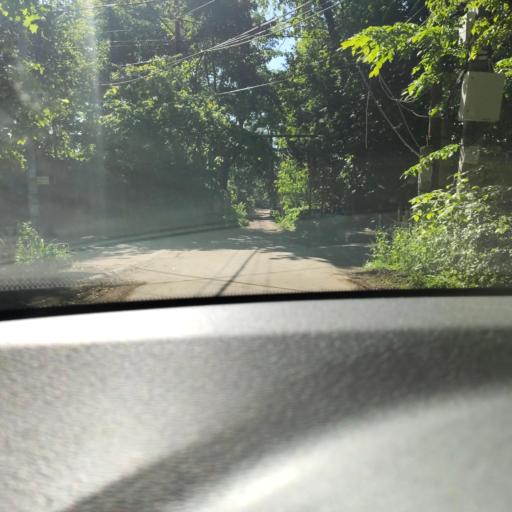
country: RU
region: Samara
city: Samara
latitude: 53.2955
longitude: 50.1957
